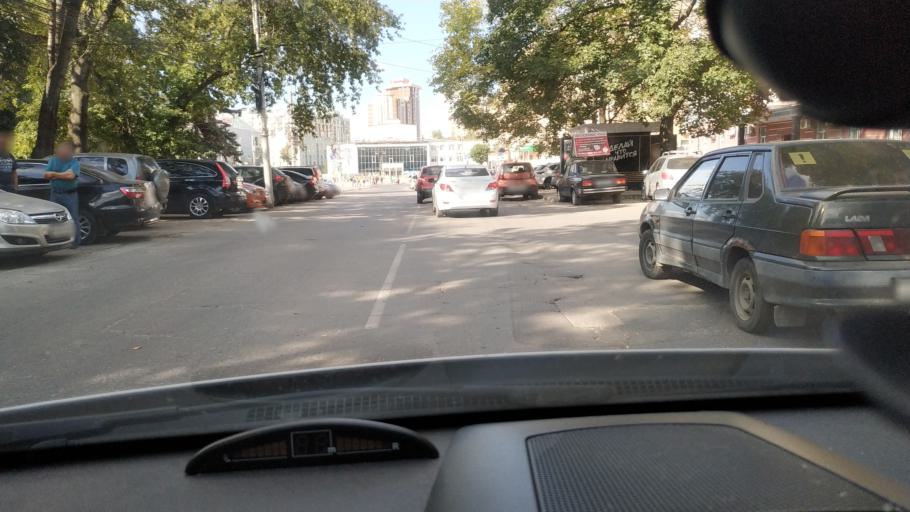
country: RU
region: Rjazan
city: Ryazan'
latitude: 54.6278
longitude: 39.7113
